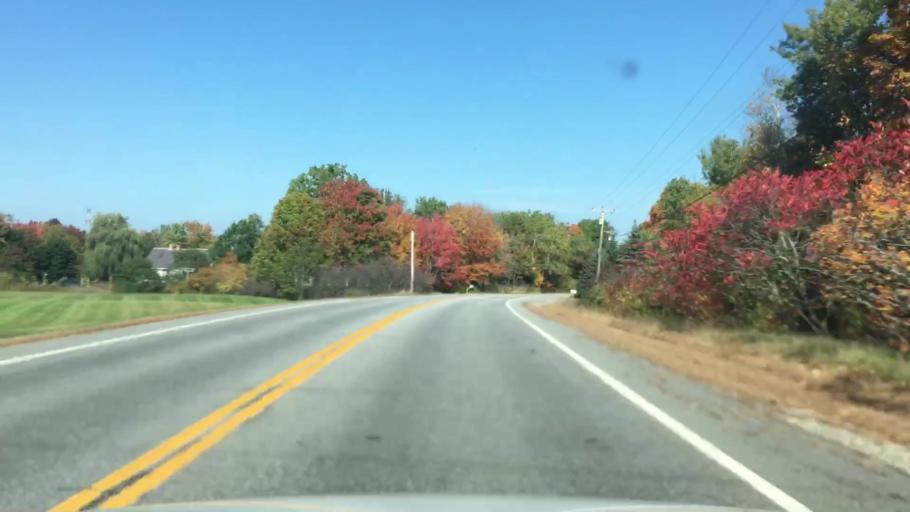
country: US
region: Maine
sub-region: Sagadahoc County
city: Topsham
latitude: 43.9778
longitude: -69.9605
